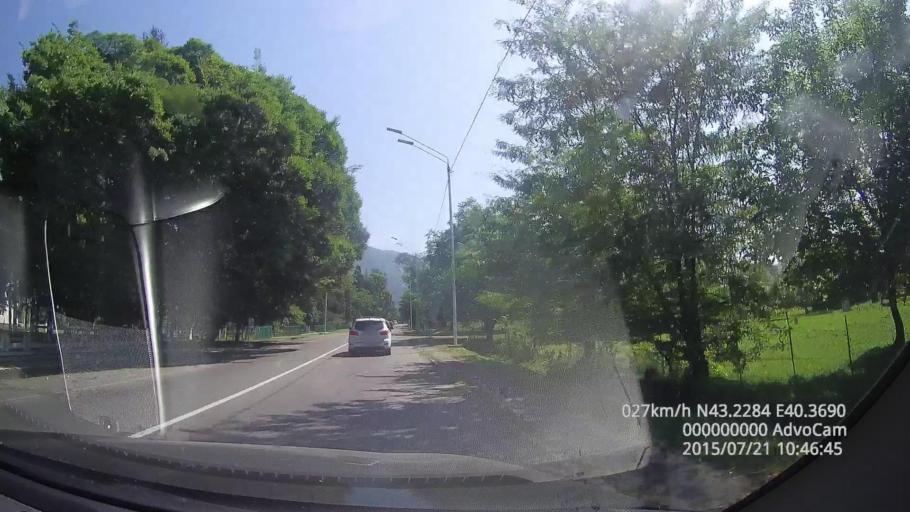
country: GE
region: Abkhazia
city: Bich'vinta
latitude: 43.2285
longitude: 40.3693
